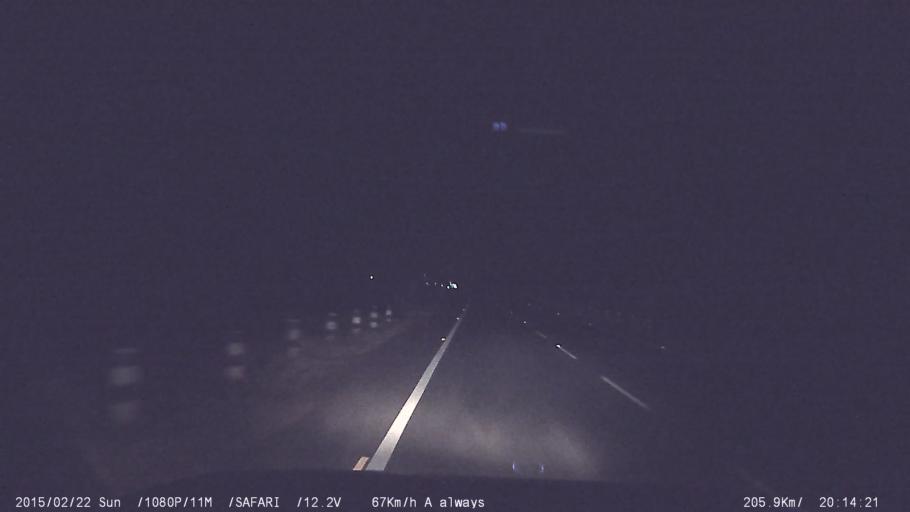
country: IN
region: Tamil Nadu
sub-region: Dindigul
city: Nilakottai
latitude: 10.2542
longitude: 77.8318
